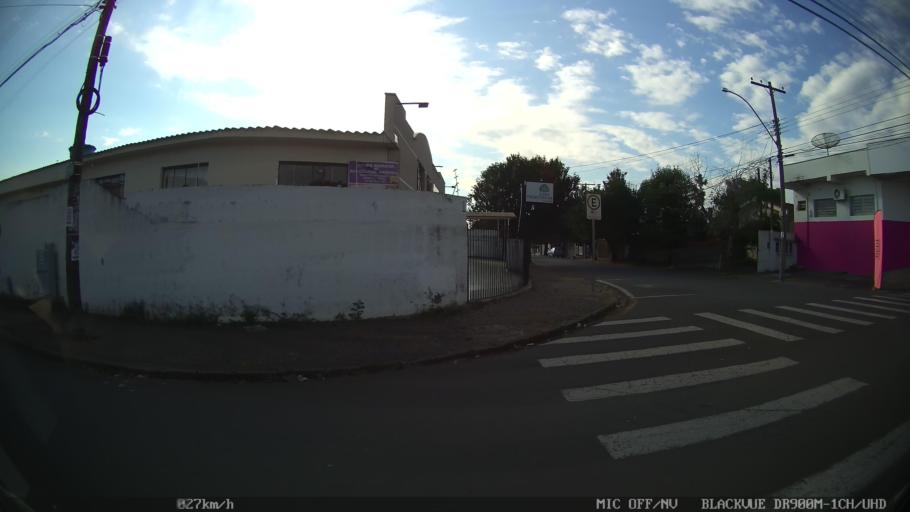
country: BR
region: Sao Paulo
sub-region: Santa Barbara D'Oeste
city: Santa Barbara d'Oeste
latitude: -22.7358
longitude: -47.3779
